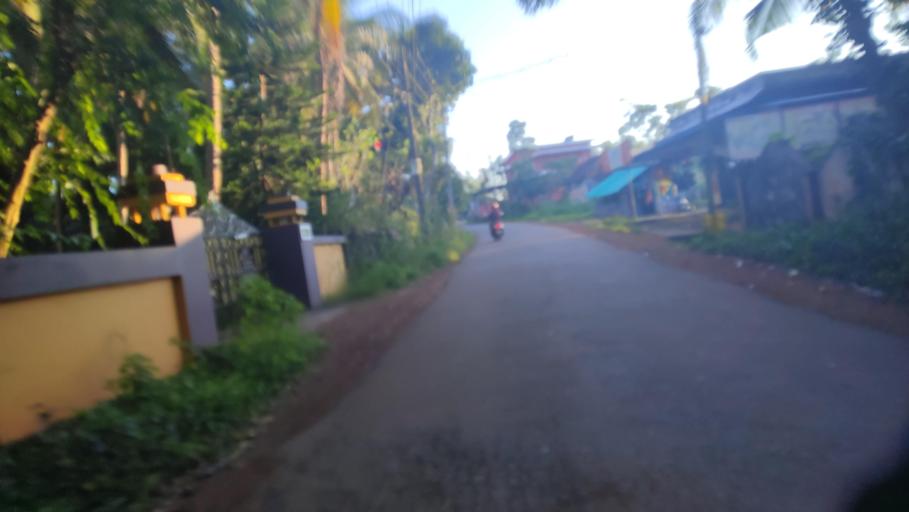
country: IN
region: Kerala
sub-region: Kasaragod District
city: Kannangad
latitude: 12.4106
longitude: 75.0950
